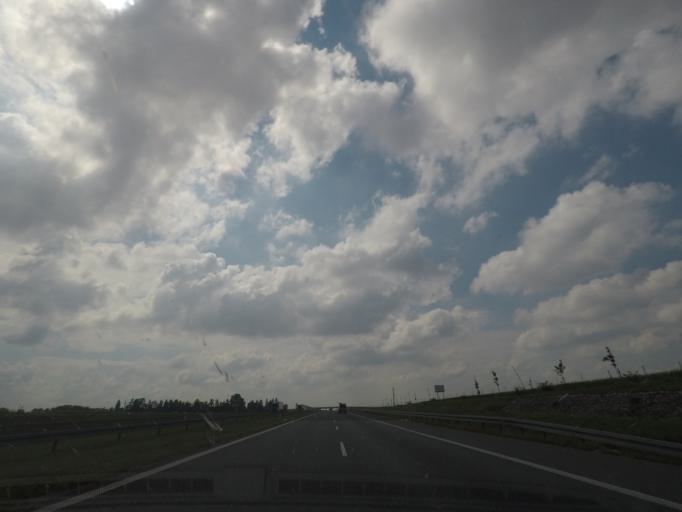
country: PL
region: Lodz Voivodeship
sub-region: Powiat kutnowski
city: Krzyzanow
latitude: 52.1626
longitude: 19.4835
